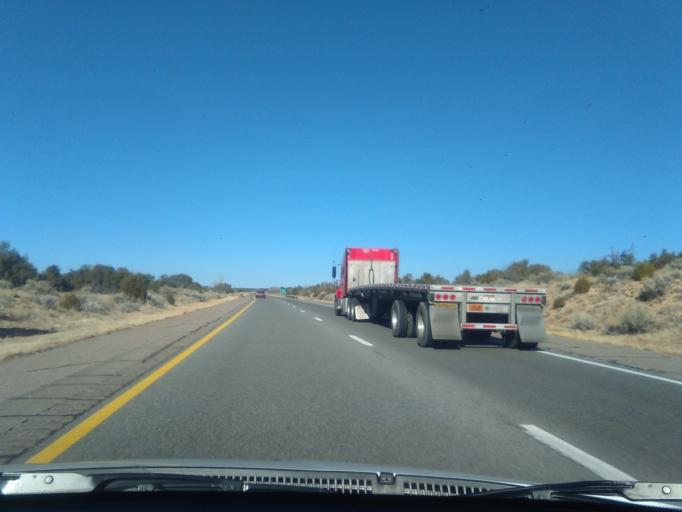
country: US
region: New Mexico
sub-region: Santa Fe County
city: Eldorado at Santa Fe
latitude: 35.5720
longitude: -105.8905
